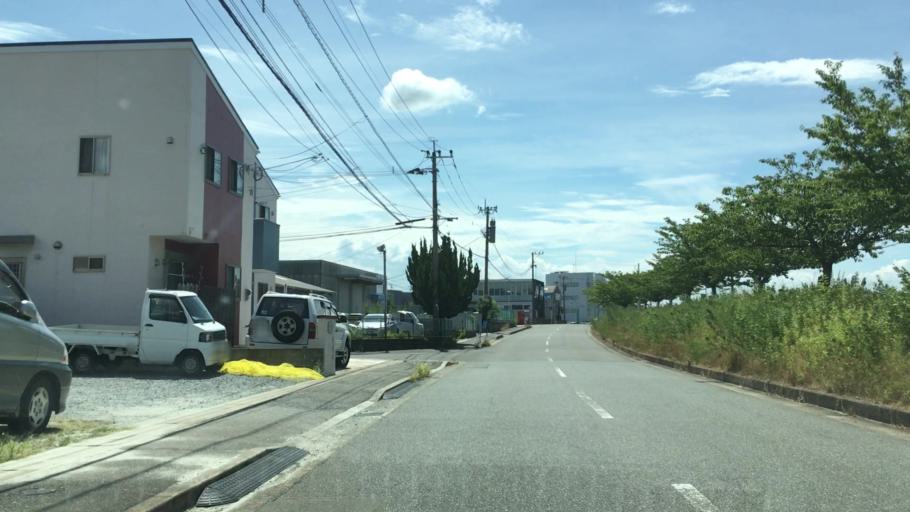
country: JP
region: Fukuoka
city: Onojo
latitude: 33.5440
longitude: 130.4817
